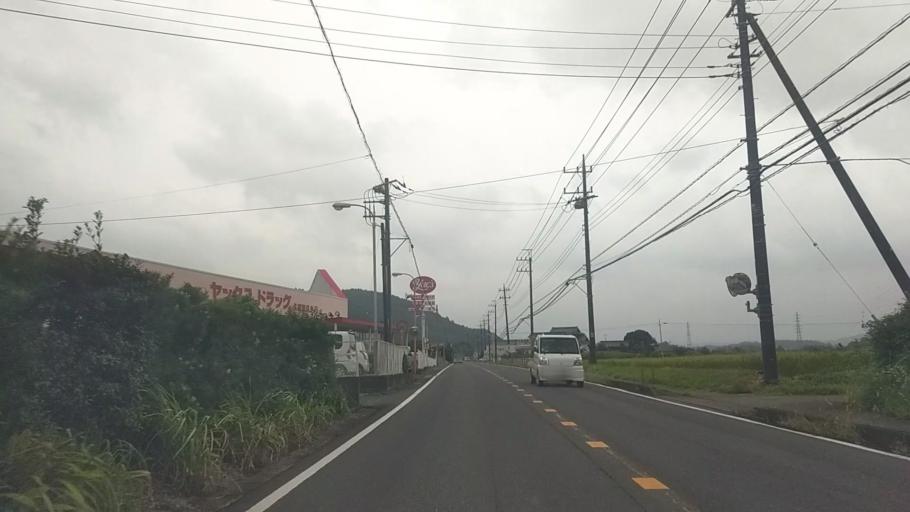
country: JP
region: Chiba
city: Kisarazu
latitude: 35.3092
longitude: 140.0660
